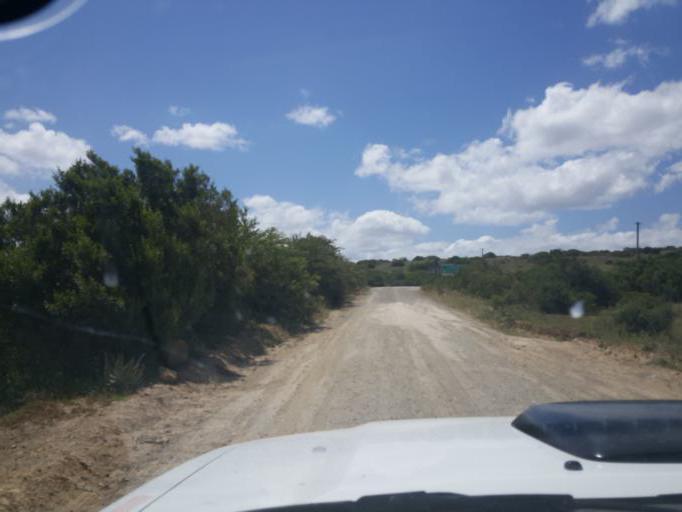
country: ZA
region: Eastern Cape
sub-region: Cacadu District Municipality
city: Grahamstown
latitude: -33.5354
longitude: 26.0866
